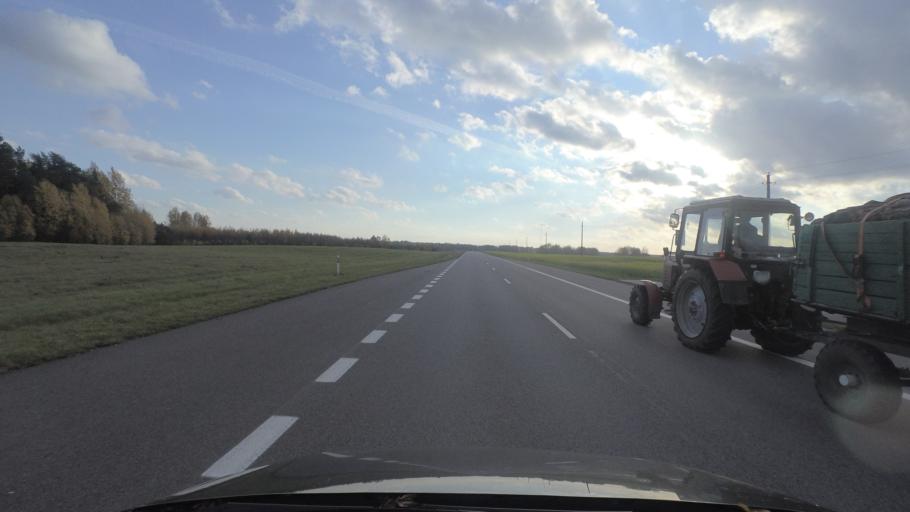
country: LT
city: Svencioneliai
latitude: 54.9818
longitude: 25.9873
